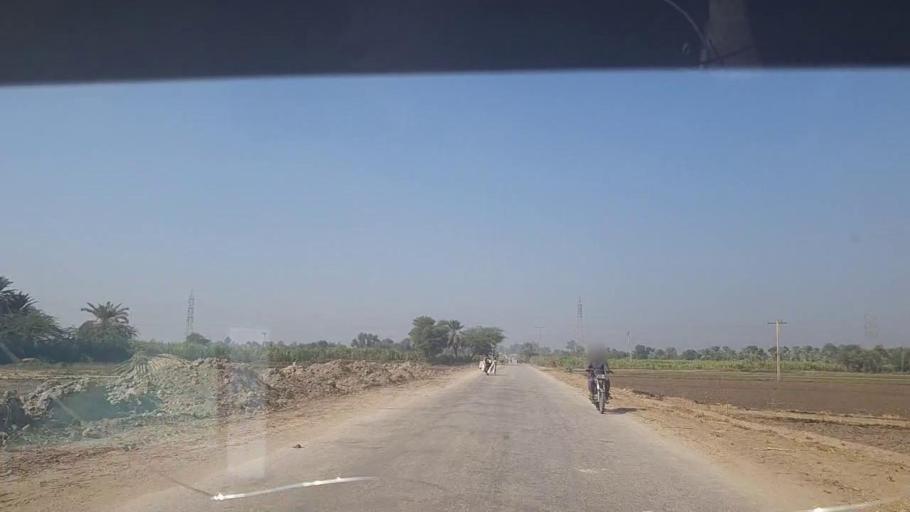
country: PK
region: Sindh
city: Kot Diji
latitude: 27.4258
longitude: 68.6566
